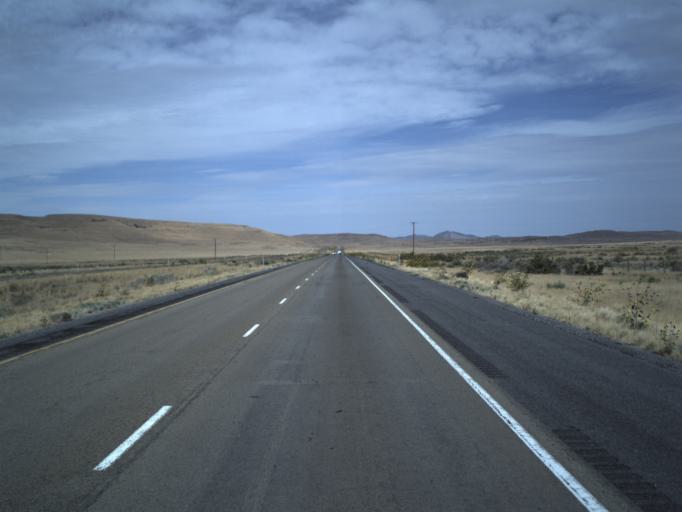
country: US
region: Utah
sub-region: Tooele County
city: Grantsville
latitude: 40.7966
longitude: -112.8427
